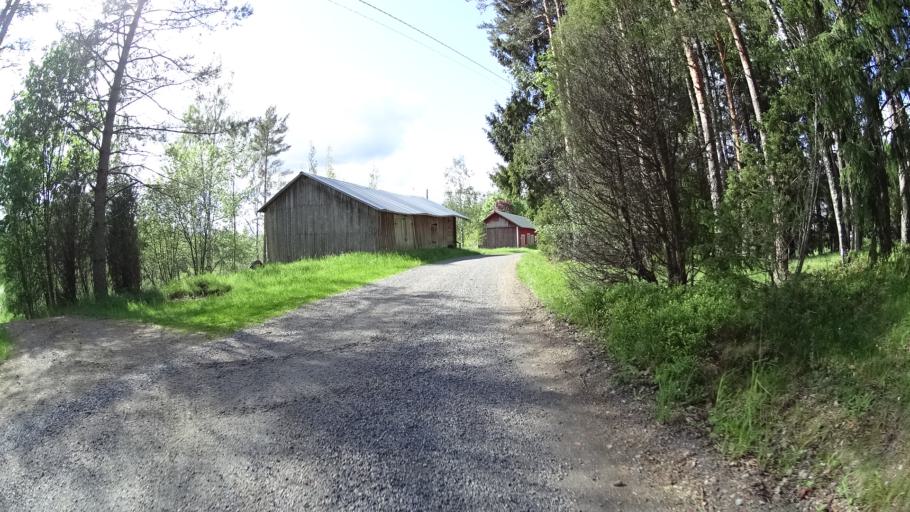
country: FI
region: Varsinais-Suomi
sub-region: Salo
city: Kisko
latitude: 60.1960
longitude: 23.5489
